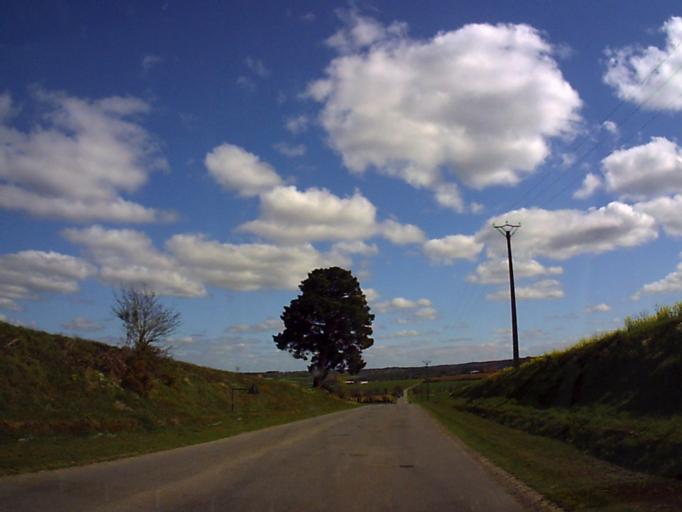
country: FR
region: Brittany
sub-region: Departement d'Ille-et-Vilaine
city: Boisgervilly
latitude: 48.1094
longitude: -2.1275
